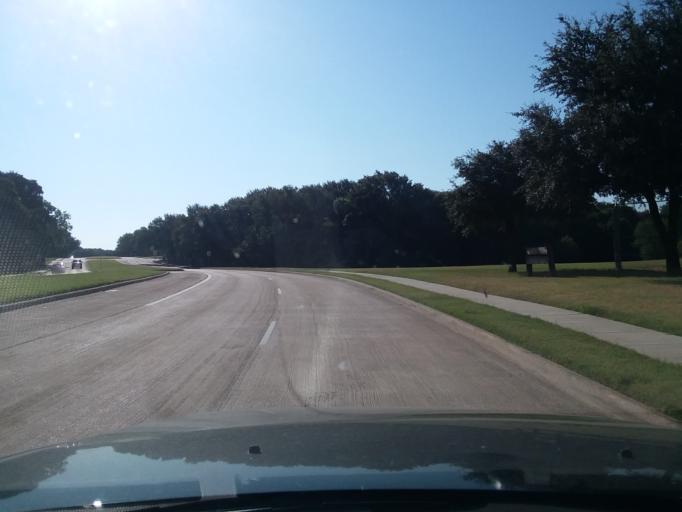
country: US
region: Texas
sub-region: Denton County
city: Double Oak
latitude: 33.0520
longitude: -97.0703
